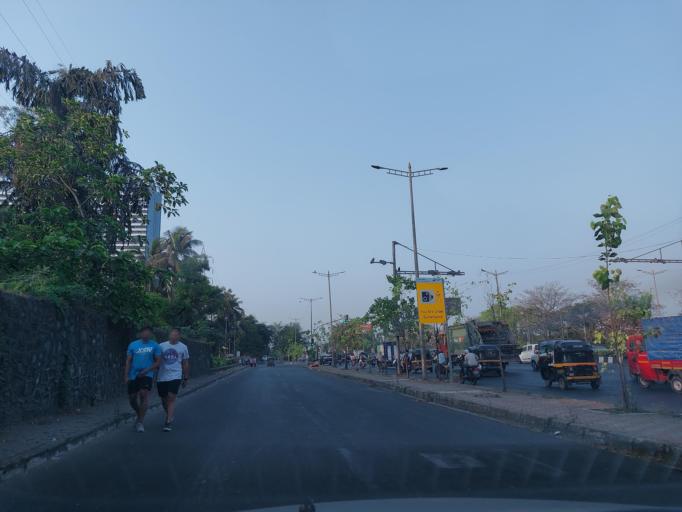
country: IN
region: Maharashtra
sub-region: Mumbai Suburban
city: Powai
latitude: 19.0998
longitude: 72.9283
